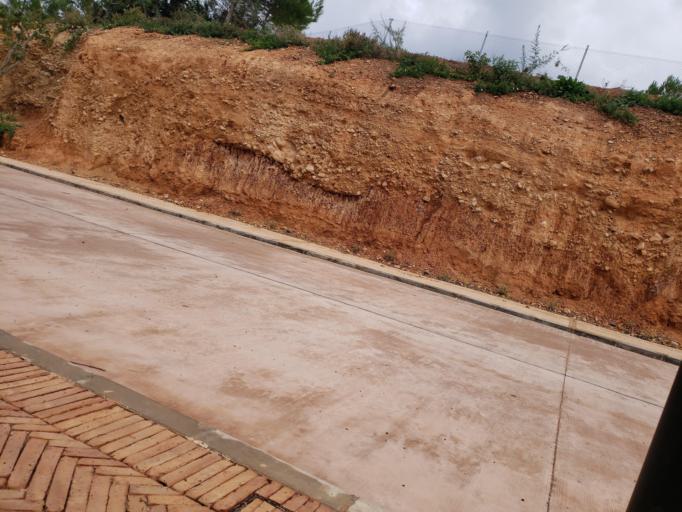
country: ES
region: Balearic Islands
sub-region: Illes Balears
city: Sant Joan de Labritja
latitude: 39.1106
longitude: 1.5088
